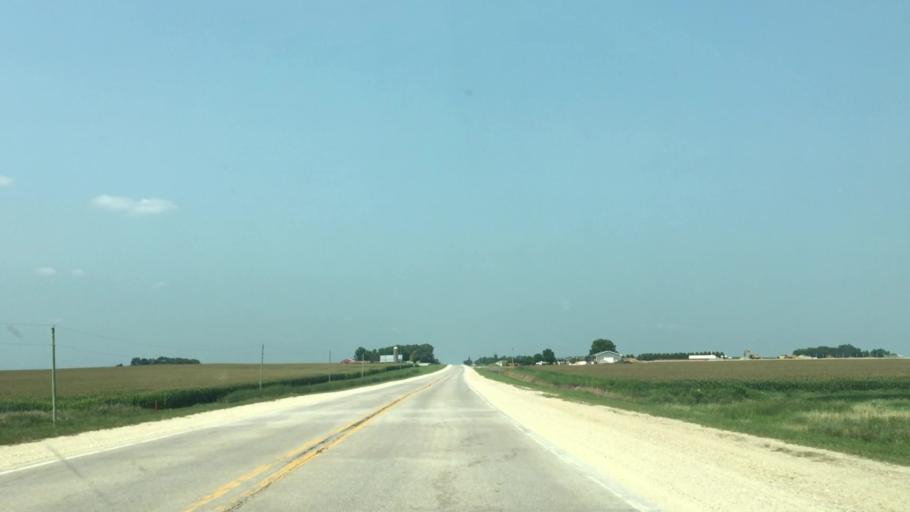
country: US
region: Iowa
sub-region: Fayette County
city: Fayette
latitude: 42.7625
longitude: -91.8045
